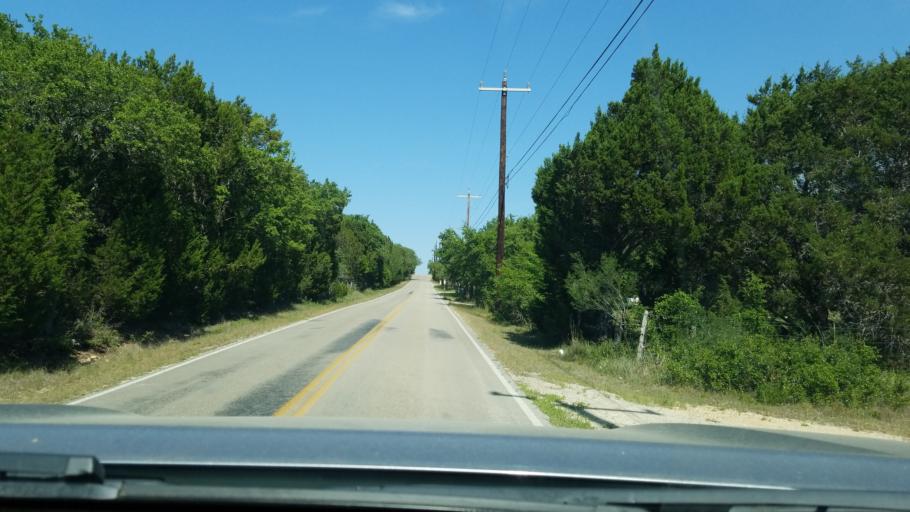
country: US
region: Texas
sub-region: Comal County
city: Bulverde
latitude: 29.7590
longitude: -98.4921
